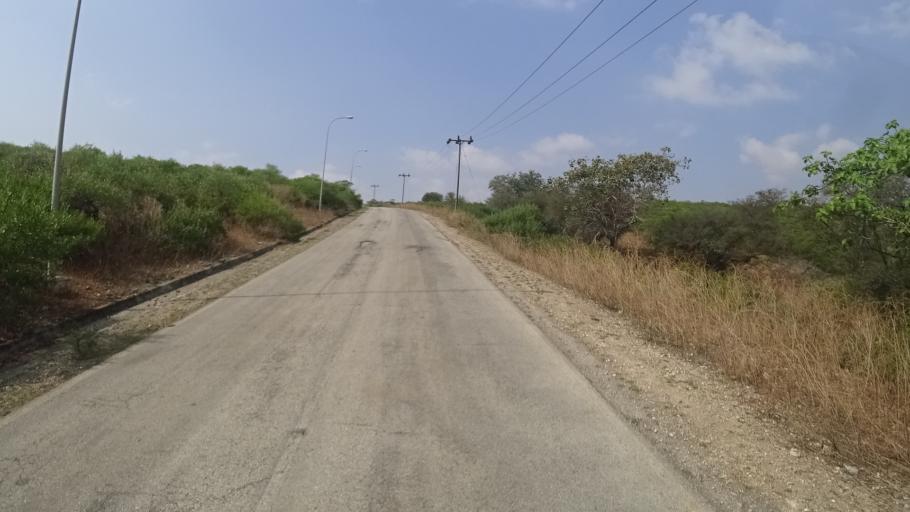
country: YE
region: Al Mahrah
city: Hawf
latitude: 16.7282
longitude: 53.2753
